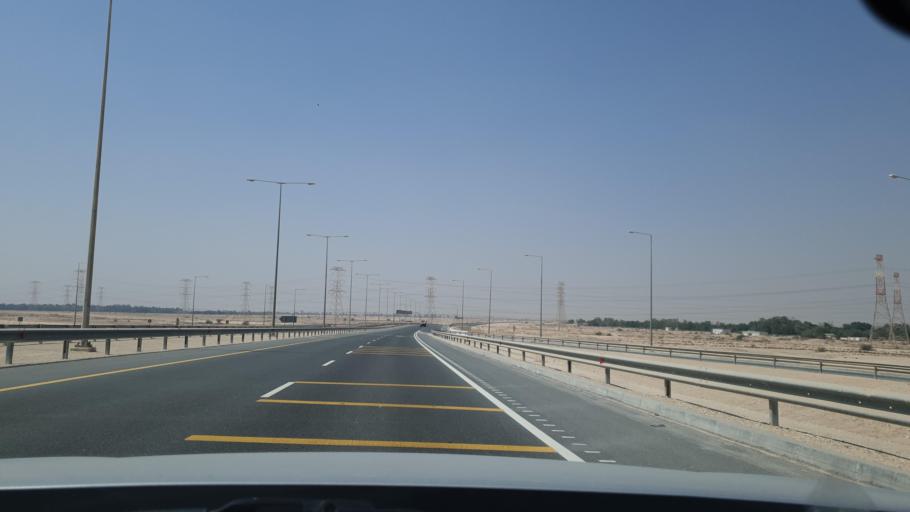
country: QA
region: Baladiyat az Za`ayin
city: Az Za`ayin
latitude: 25.6174
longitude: 51.3636
